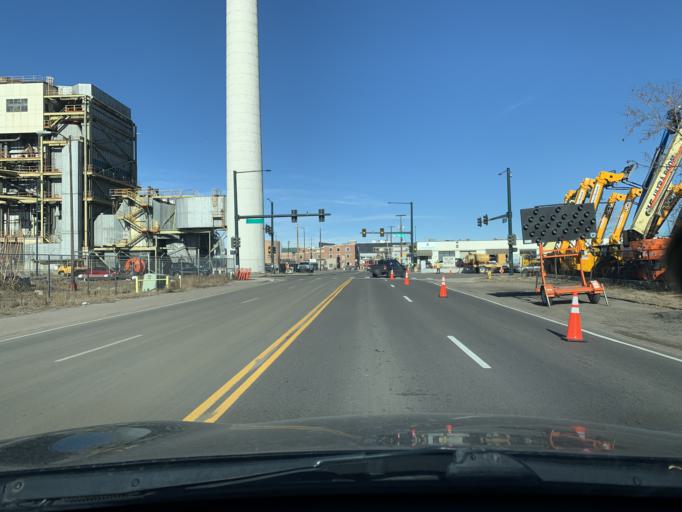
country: US
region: Colorado
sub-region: Denver County
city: Denver
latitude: 39.7363
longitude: -105.0160
